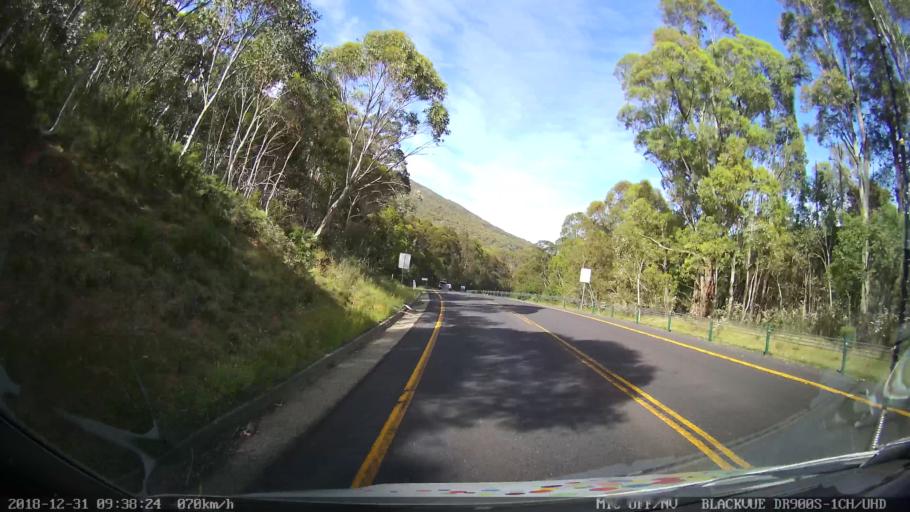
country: AU
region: New South Wales
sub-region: Snowy River
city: Jindabyne
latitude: -36.4740
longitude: 148.3680
